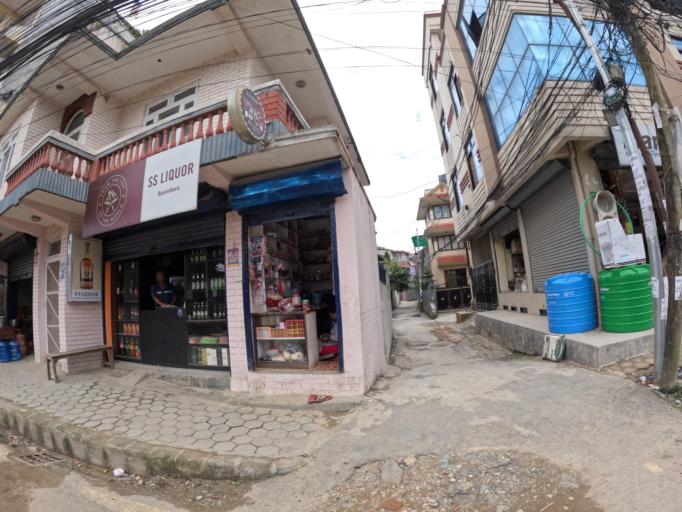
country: NP
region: Central Region
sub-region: Bagmati Zone
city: Kathmandu
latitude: 27.7440
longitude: 85.3337
